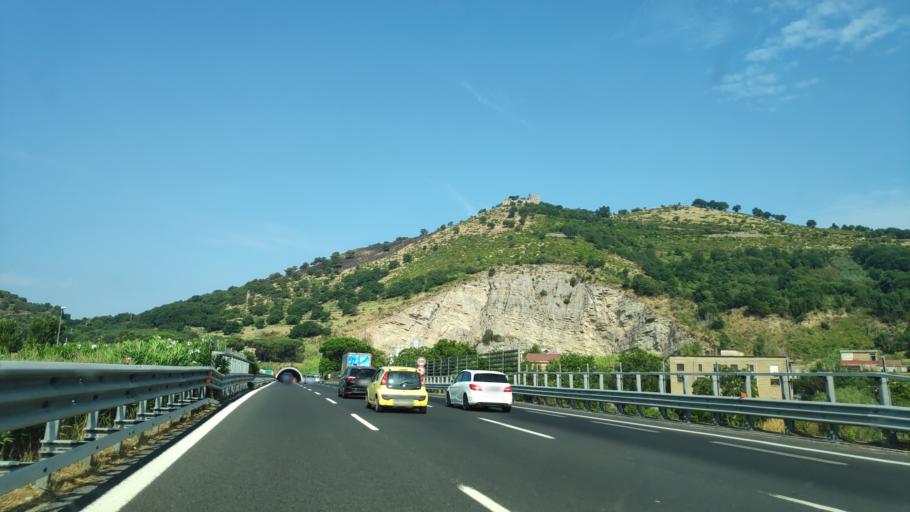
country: IT
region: Campania
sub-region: Provincia di Salerno
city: Lanzara
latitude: 40.7717
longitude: 14.6648
